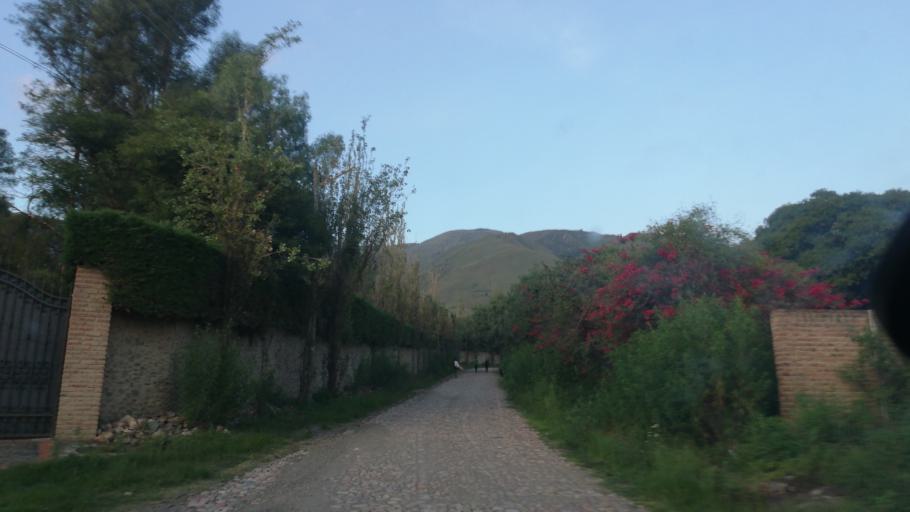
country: BO
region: Cochabamba
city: Cochabamba
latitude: -17.3349
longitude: -66.2094
